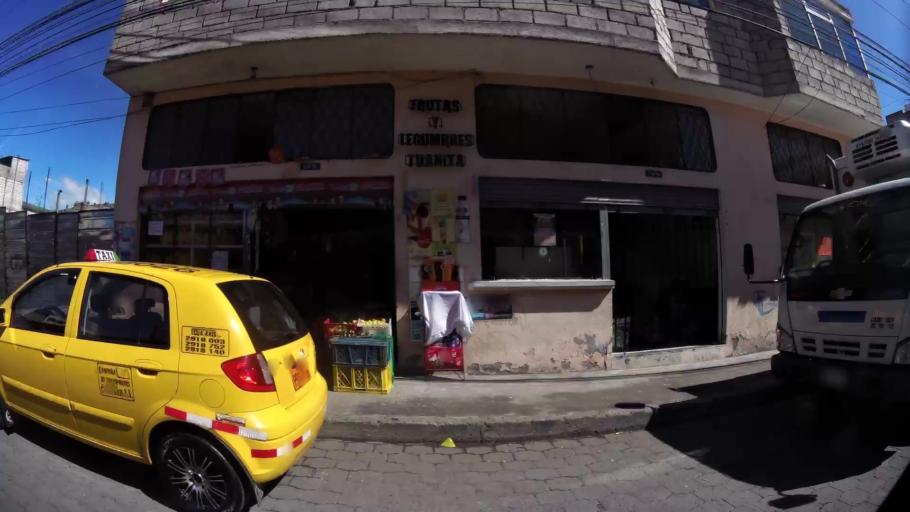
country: EC
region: Pichincha
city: Quito
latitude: -0.2773
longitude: -78.5555
